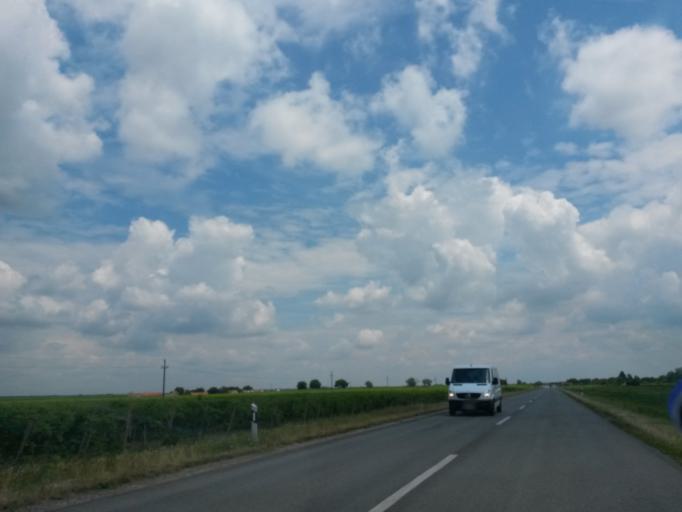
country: HR
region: Osjecko-Baranjska
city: Dalj
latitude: 45.5046
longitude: 19.0054
